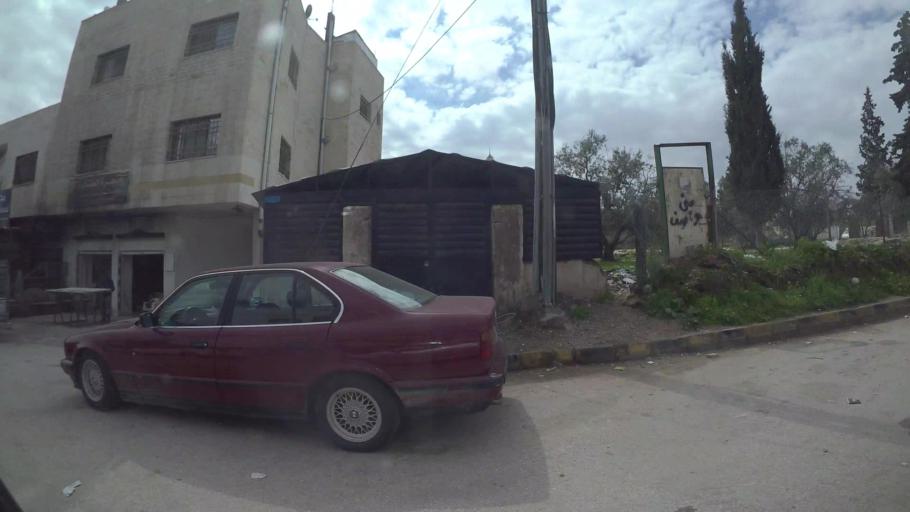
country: JO
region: Amman
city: Al Jubayhah
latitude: 32.0586
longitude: 35.8277
